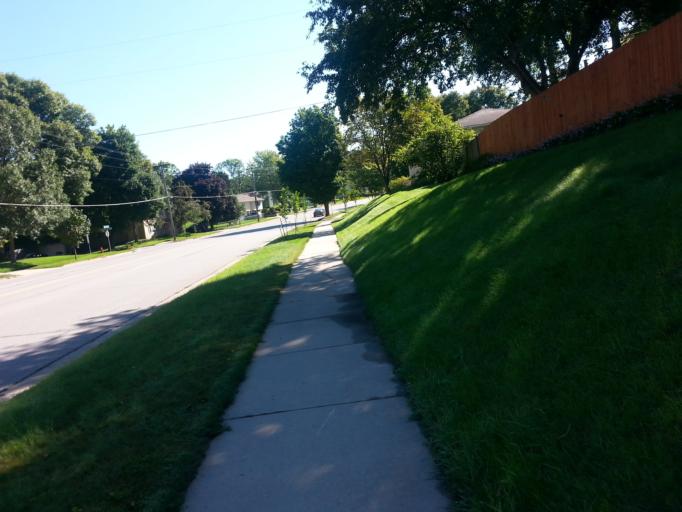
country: US
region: Minnesota
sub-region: Olmsted County
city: Rochester
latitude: 44.0498
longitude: -92.4762
